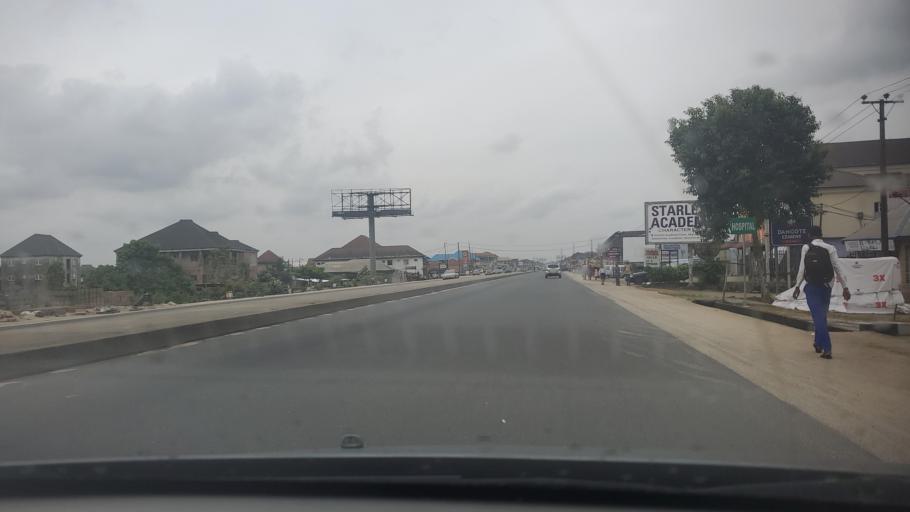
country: NG
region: Rivers
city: Port Harcourt
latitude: 4.8698
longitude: 6.9759
